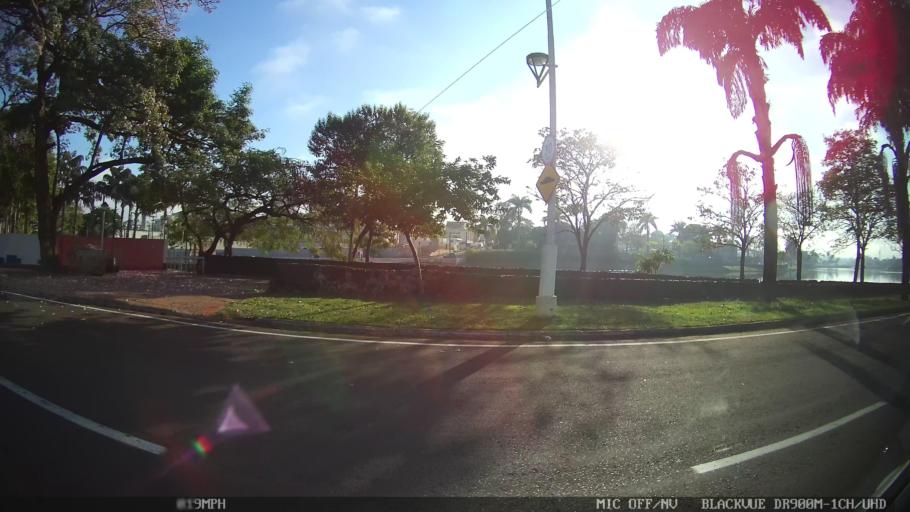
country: BR
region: Sao Paulo
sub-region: Sao Jose Do Rio Preto
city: Sao Jose do Rio Preto
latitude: -20.8095
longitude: -49.3740
